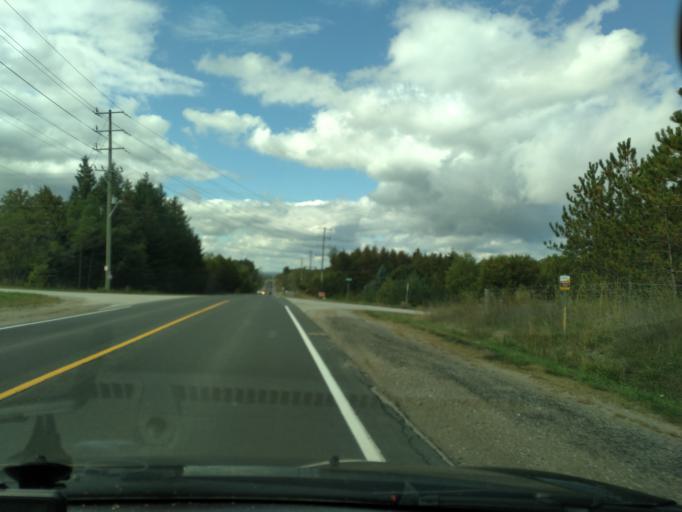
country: CA
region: Ontario
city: Innisfil
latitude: 44.2647
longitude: -79.7496
